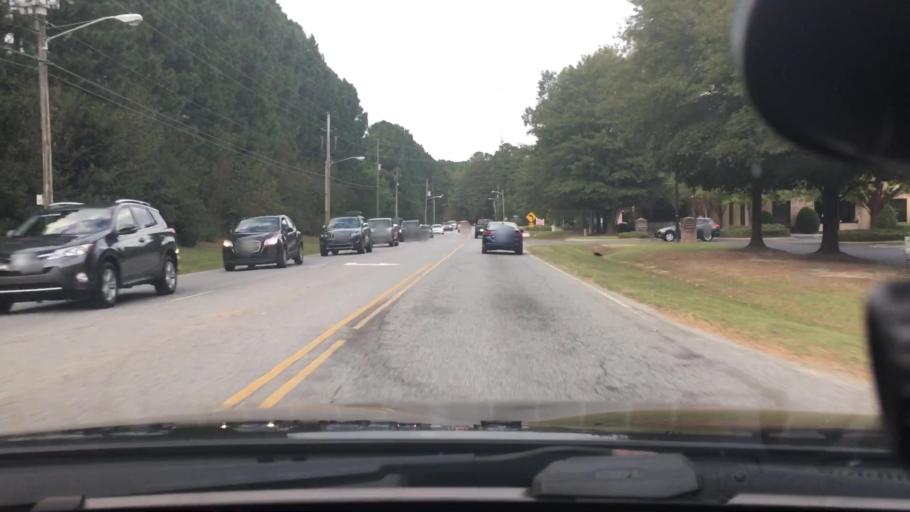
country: US
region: North Carolina
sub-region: Pitt County
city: Summerfield
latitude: 35.5653
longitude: -77.3842
